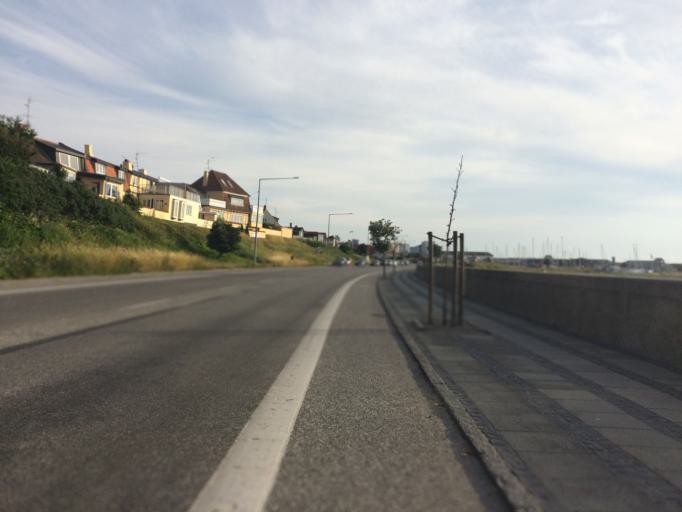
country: DK
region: Capital Region
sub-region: Bornholm Kommune
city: Ronne
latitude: 55.1051
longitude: 14.6974
